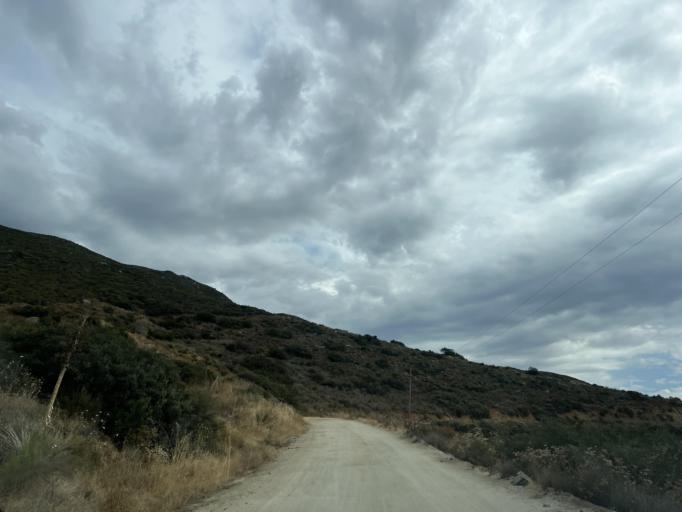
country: US
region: California
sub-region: San Diego County
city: Alpine
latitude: 32.8582
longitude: -116.7425
